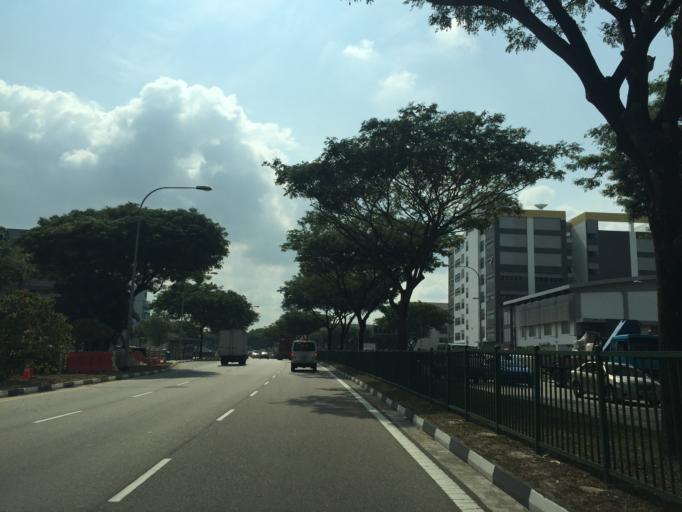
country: SG
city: Singapore
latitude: 1.3346
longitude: 103.8918
